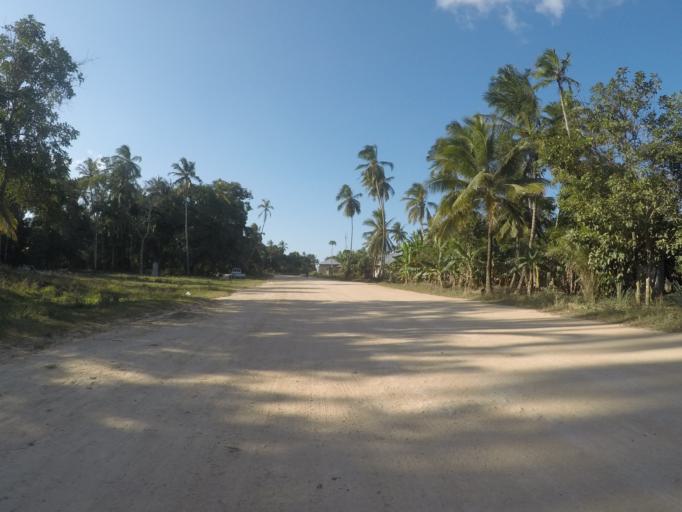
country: TZ
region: Zanzibar Central/South
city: Koani
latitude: -6.1630
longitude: 39.2872
